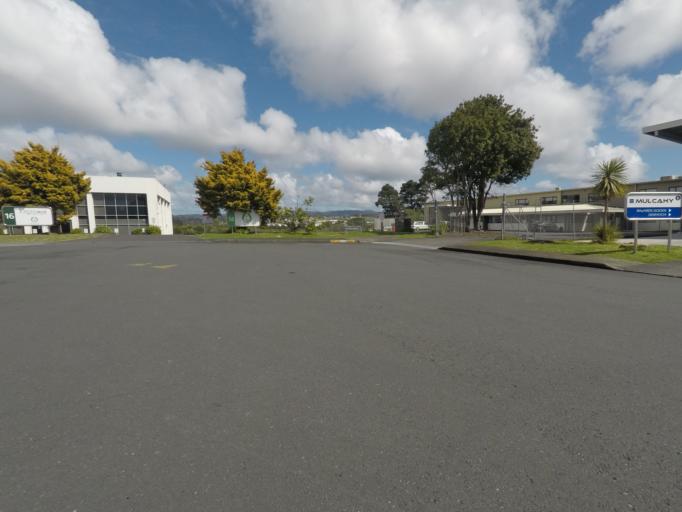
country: NZ
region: Auckland
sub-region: Auckland
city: Rosebank
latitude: -36.8818
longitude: 174.6733
